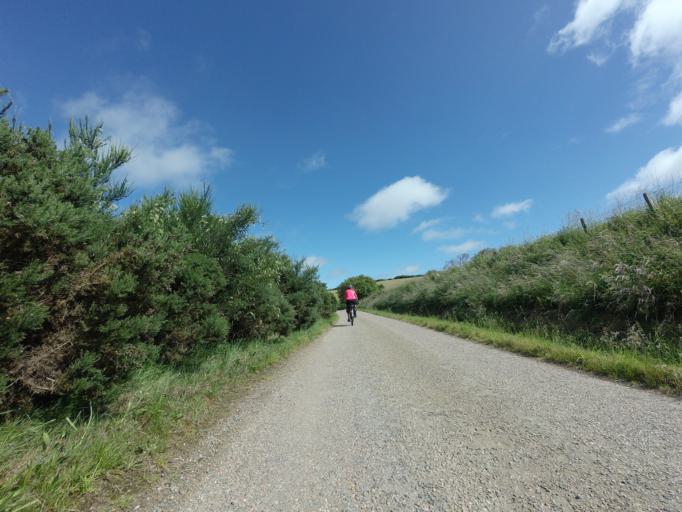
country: GB
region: Scotland
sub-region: Aberdeenshire
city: Banff
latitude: 57.6001
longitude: -2.5118
